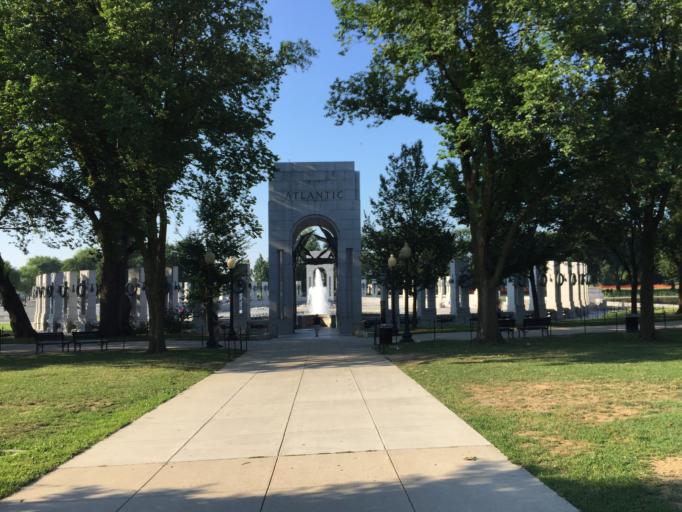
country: US
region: Washington, D.C.
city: Washington, D.C.
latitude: 38.8903
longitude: -77.0406
